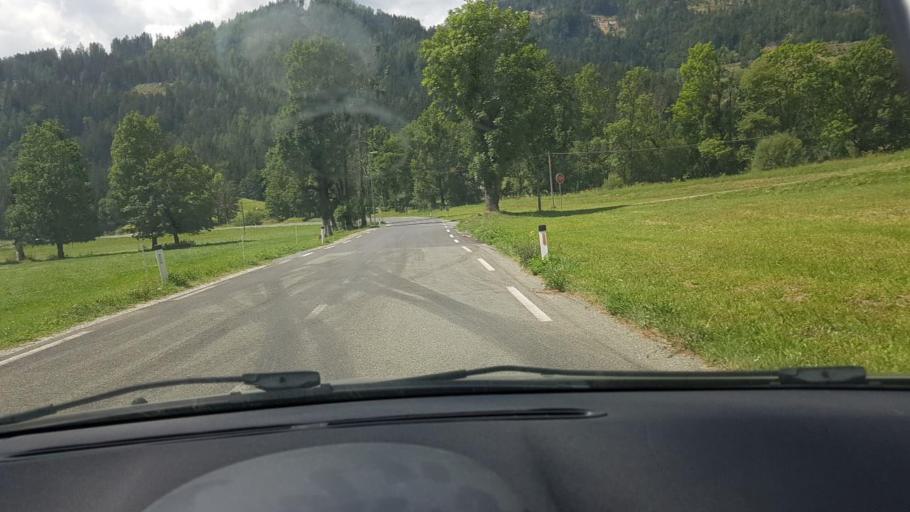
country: SI
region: Jezersko
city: Zgornje Jezersko
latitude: 46.4065
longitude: 14.5131
